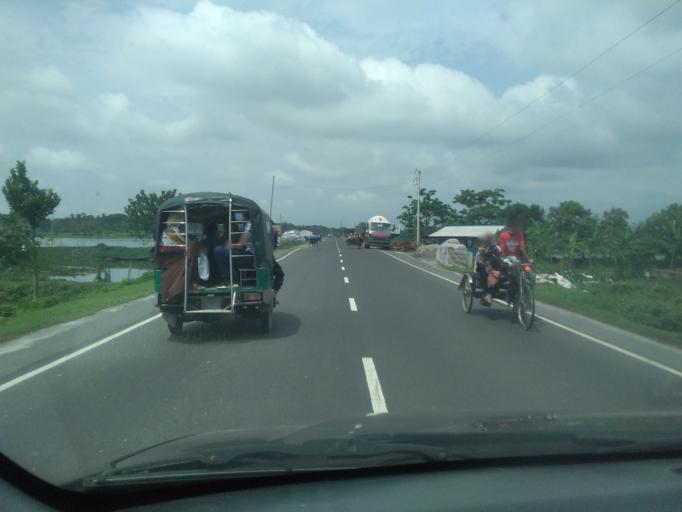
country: BD
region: Khulna
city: Kesabpur
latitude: 22.7867
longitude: 89.2141
